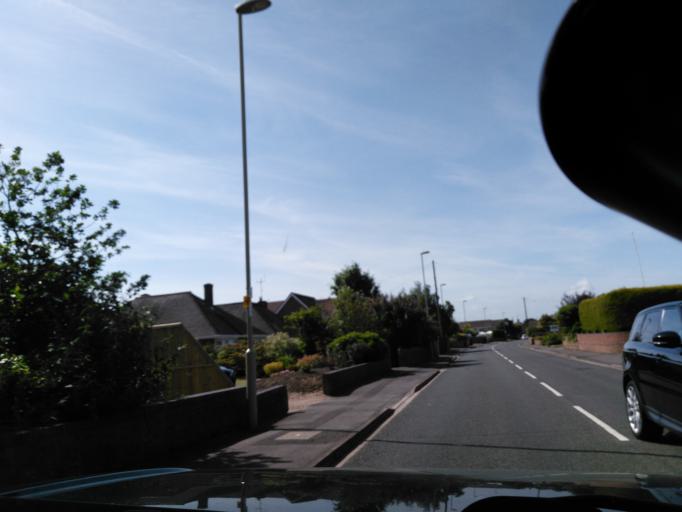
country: GB
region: England
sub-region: Hampshire
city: Lee-on-the-Solent
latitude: 50.8184
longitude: -1.2128
